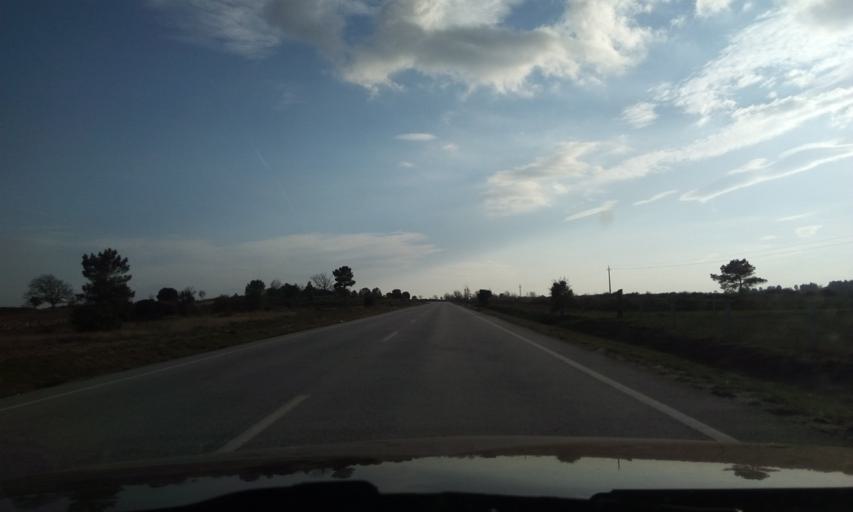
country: ES
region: Castille and Leon
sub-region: Provincia de Salamanca
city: Fuentes de Onoro
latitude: 40.6197
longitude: -6.9790
